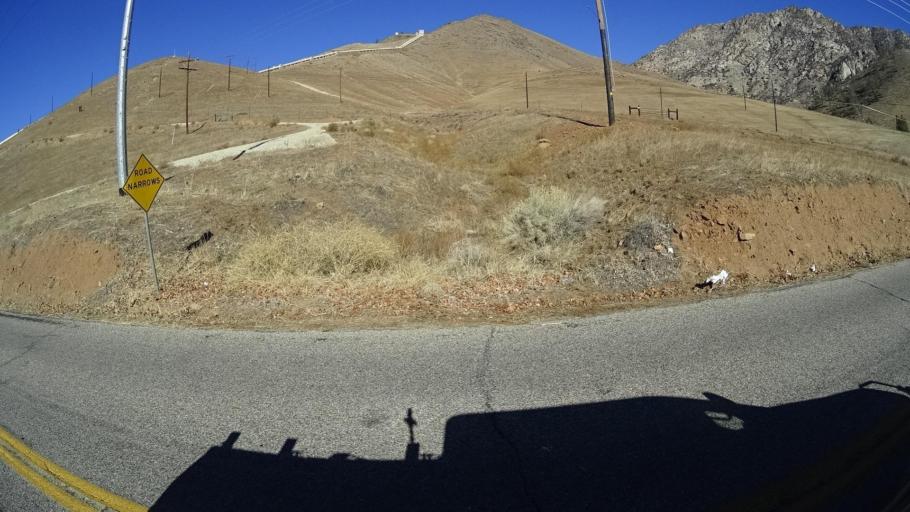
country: US
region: California
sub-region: Kern County
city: Kernville
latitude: 35.7750
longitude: -118.4336
